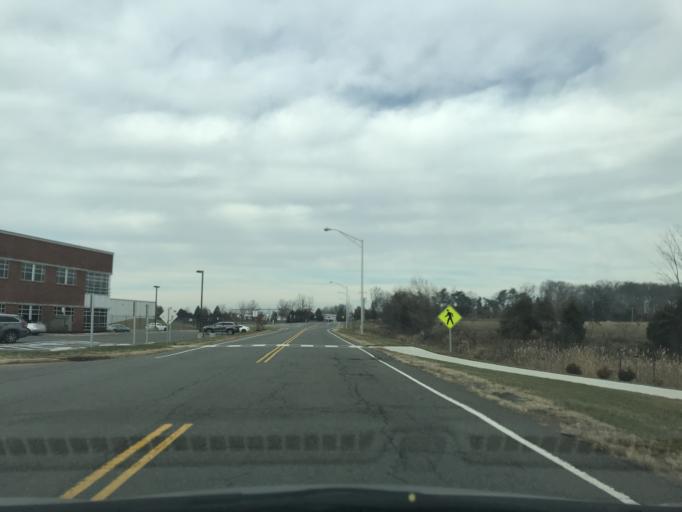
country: US
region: Virginia
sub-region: City of Manassas
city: Manassas
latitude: 38.7320
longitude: -77.5157
